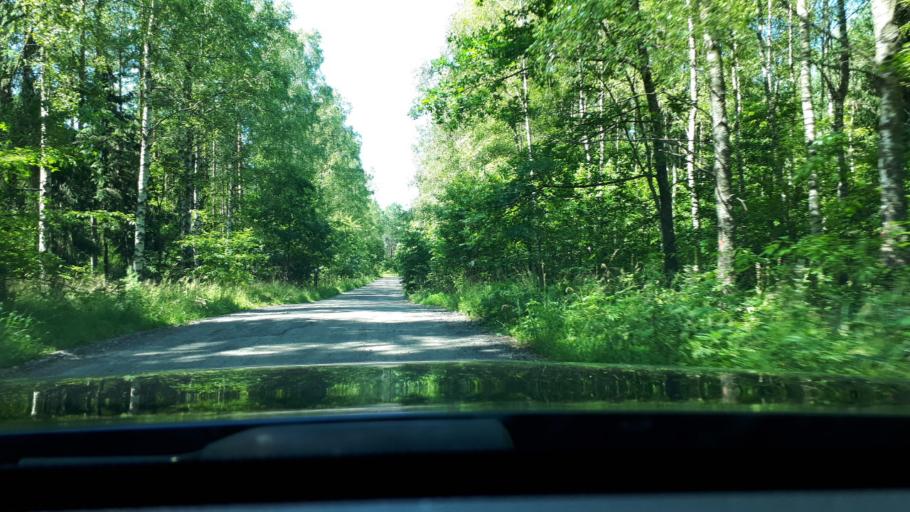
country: PL
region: Warmian-Masurian Voivodeship
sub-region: Powiat olsztynski
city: Gietrzwald
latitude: 53.6922
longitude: 20.2234
